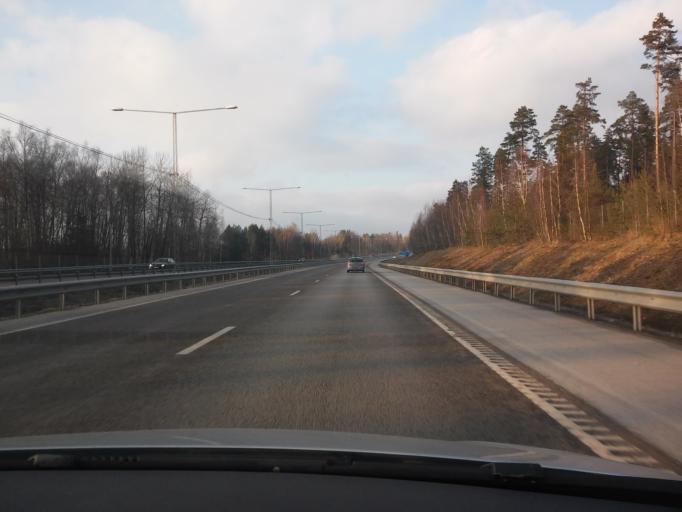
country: SE
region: Stockholm
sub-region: Vallentuna Kommun
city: Vallentuna
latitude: 59.4905
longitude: 18.1648
